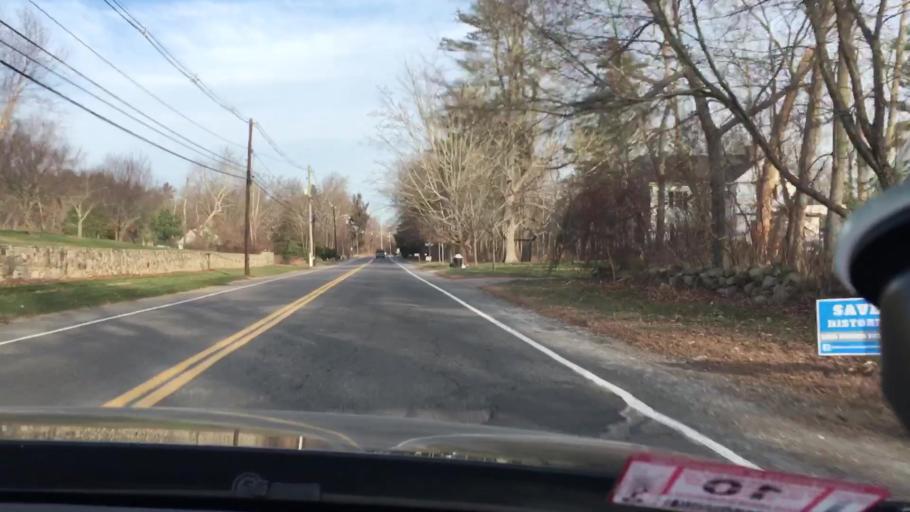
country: US
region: Massachusetts
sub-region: Norfolk County
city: Walpole
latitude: 42.1800
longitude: -71.2444
